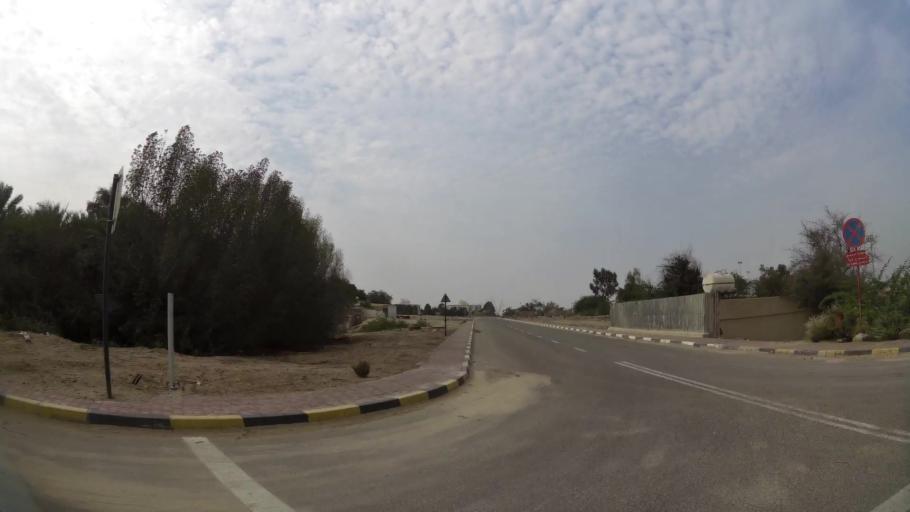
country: AE
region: Abu Dhabi
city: Abu Dhabi
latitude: 24.6873
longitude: 54.7676
